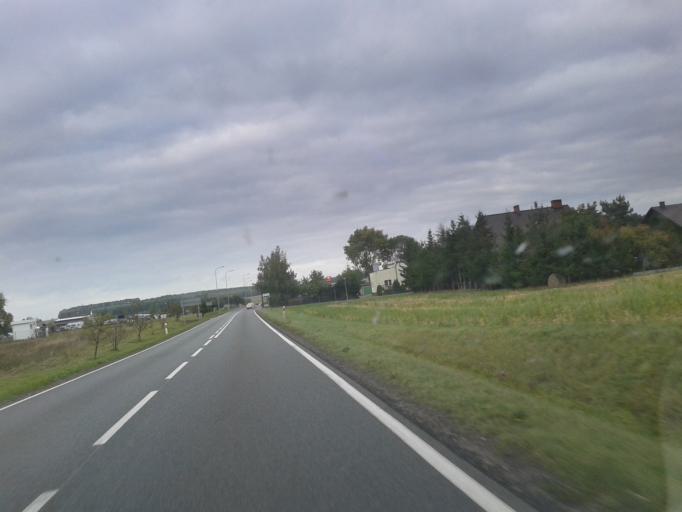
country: PL
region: Kujawsko-Pomorskie
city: Kamien Krajenski
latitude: 53.5276
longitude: 17.5120
